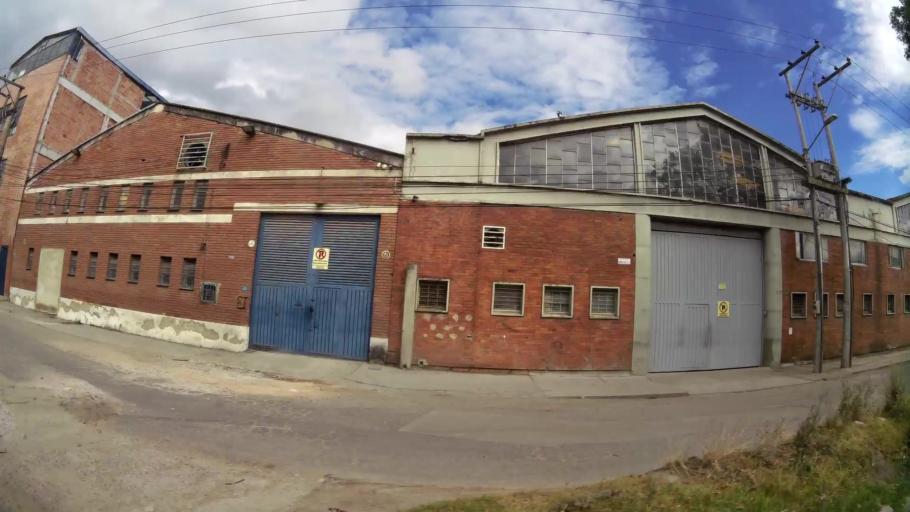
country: CO
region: Bogota D.C.
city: Bogota
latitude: 4.6239
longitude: -74.0997
